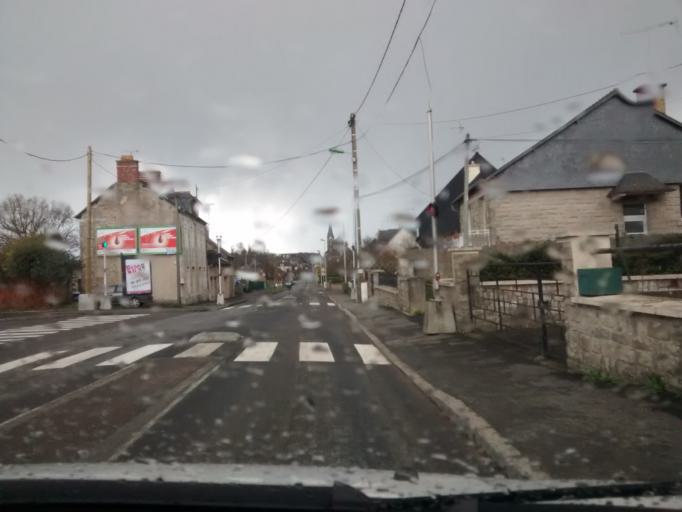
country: FR
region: Brittany
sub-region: Departement d'Ille-et-Vilaine
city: Liffre
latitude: 48.2094
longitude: -1.5021
